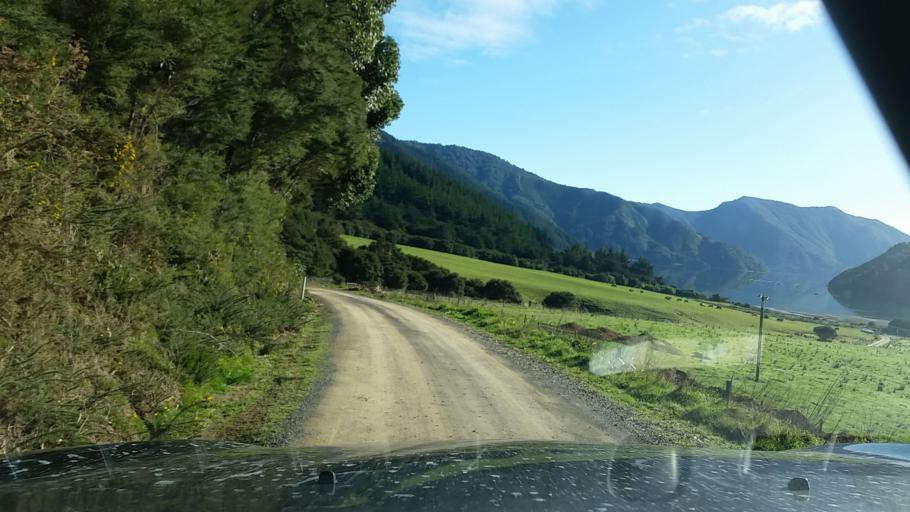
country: NZ
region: Marlborough
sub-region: Marlborough District
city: Picton
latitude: -41.1546
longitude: 173.9688
